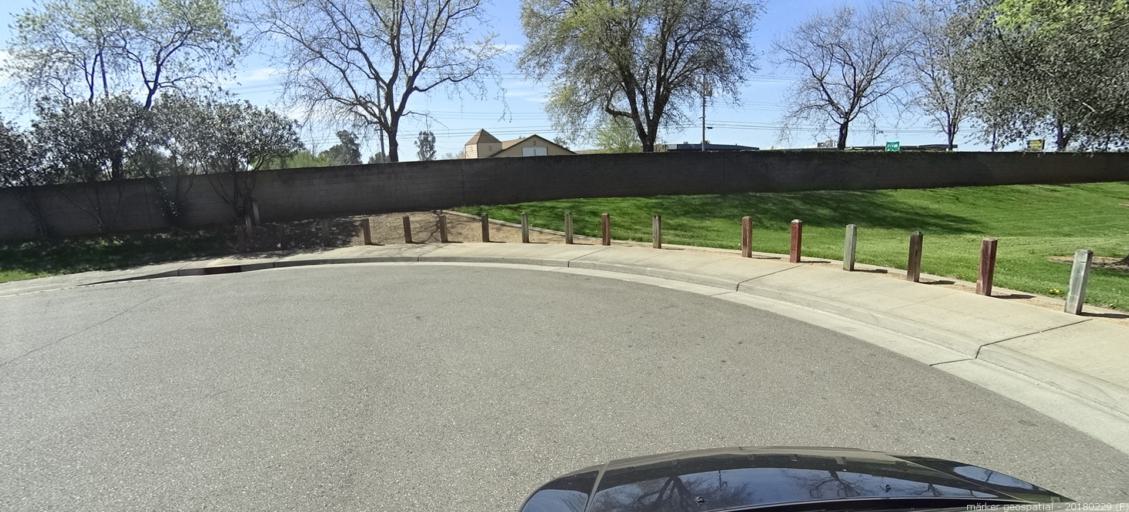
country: US
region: California
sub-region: Sacramento County
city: Rosemont
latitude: 38.5361
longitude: -121.3601
